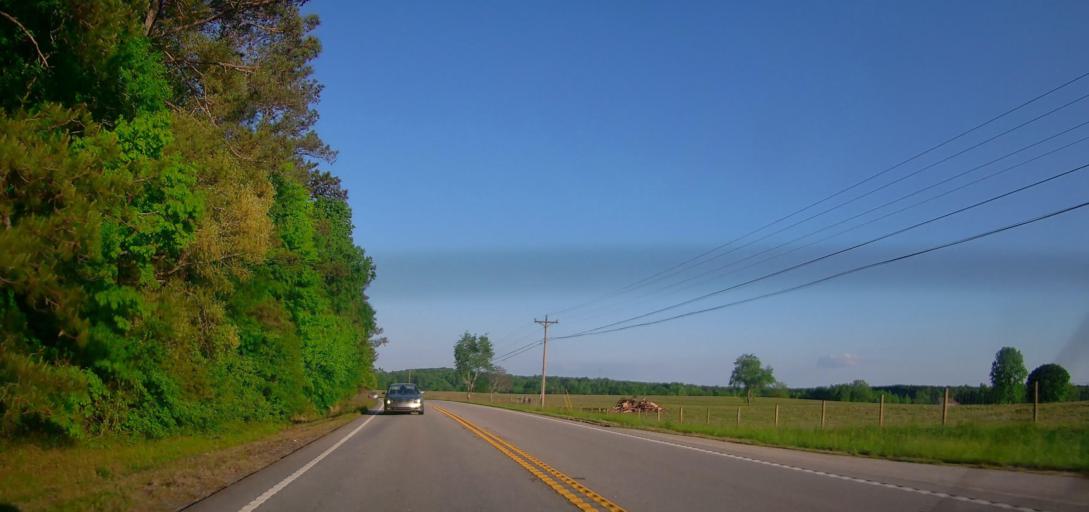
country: US
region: Georgia
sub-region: Walton County
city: Social Circle
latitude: 33.5367
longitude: -83.7226
